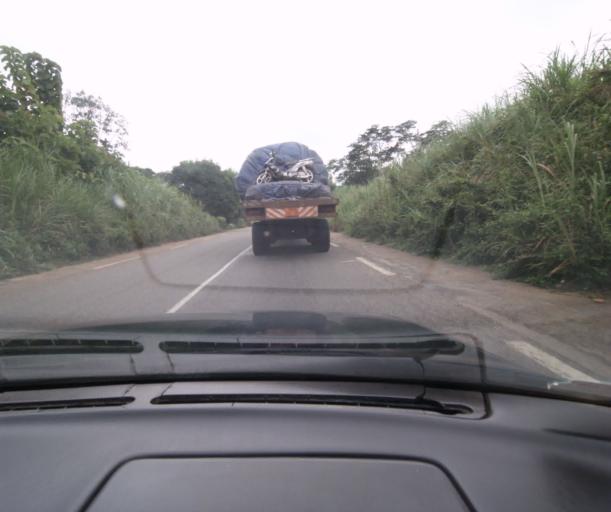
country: CM
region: Centre
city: Ombesa
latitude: 4.5737
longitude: 11.2666
